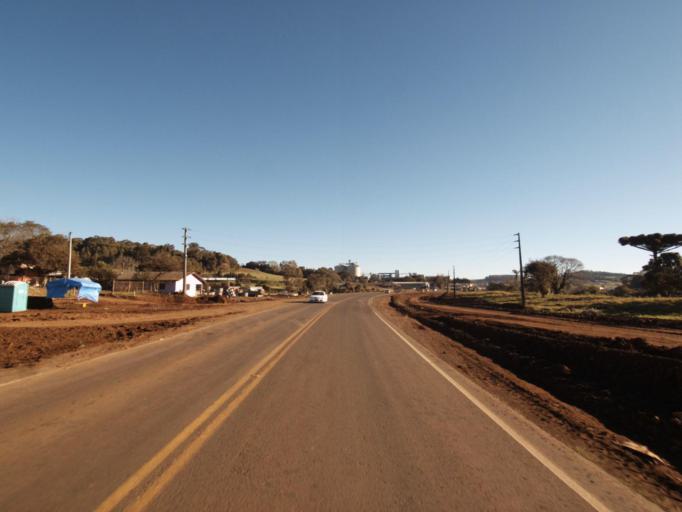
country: AR
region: Misiones
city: Bernardo de Irigoyen
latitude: -26.4599
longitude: -53.5097
